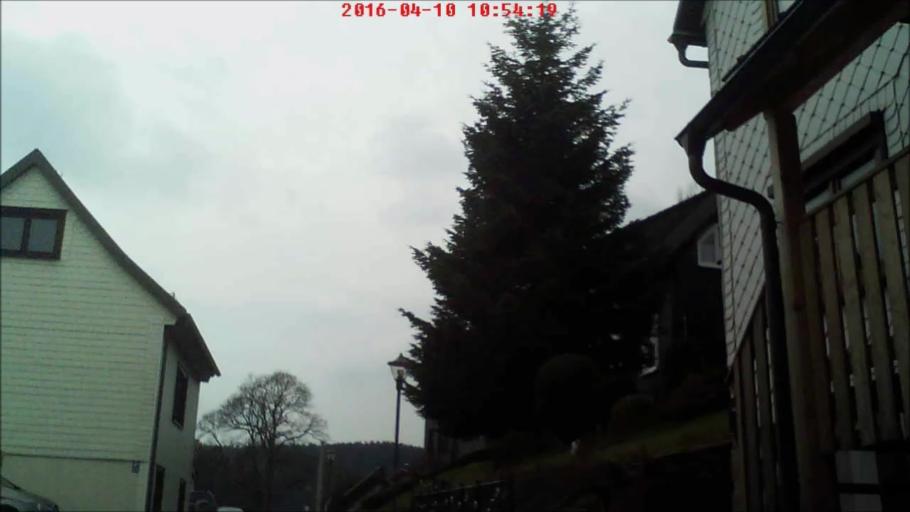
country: DE
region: Thuringia
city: Stutzerbach
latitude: 50.6305
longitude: 10.8592
